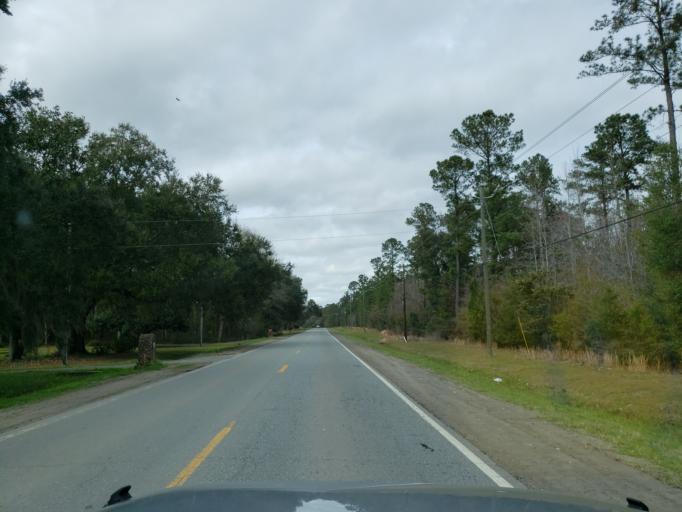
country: US
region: Georgia
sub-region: Chatham County
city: Georgetown
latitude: 32.0213
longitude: -81.2646
